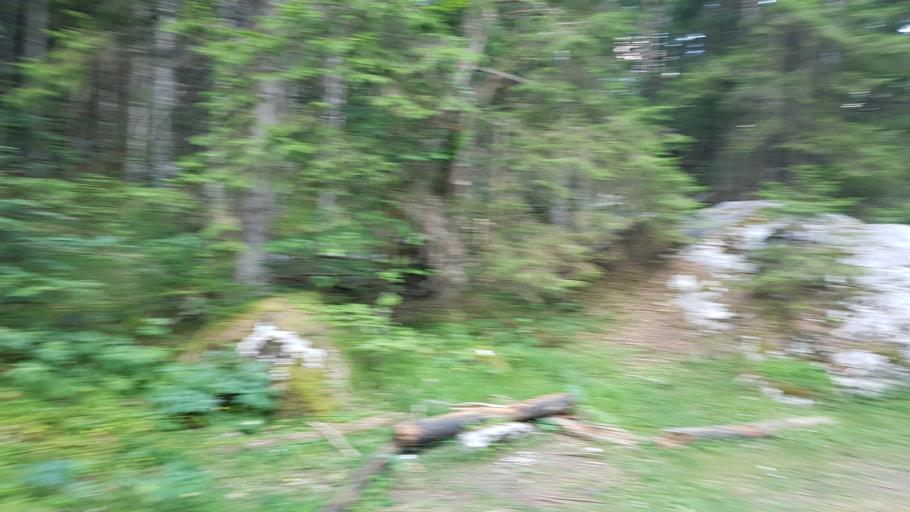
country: SI
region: Kranjska Gora
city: Kranjska Gora
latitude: 46.3614
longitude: 13.7534
